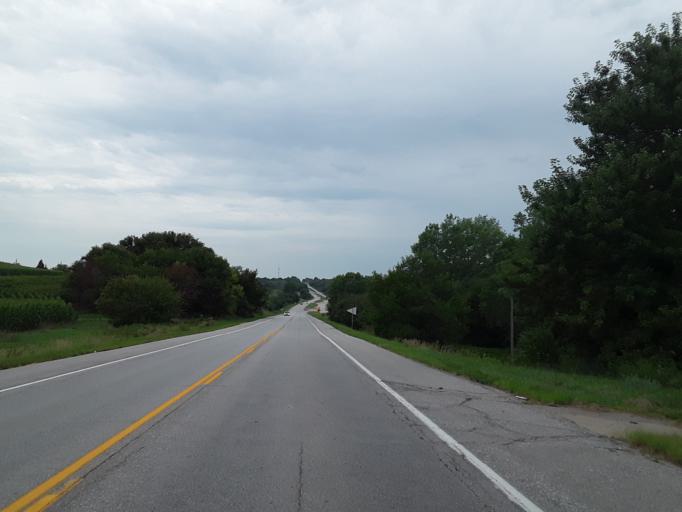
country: US
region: Nebraska
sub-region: Douglas County
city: Bennington
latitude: 41.3647
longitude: -96.0390
